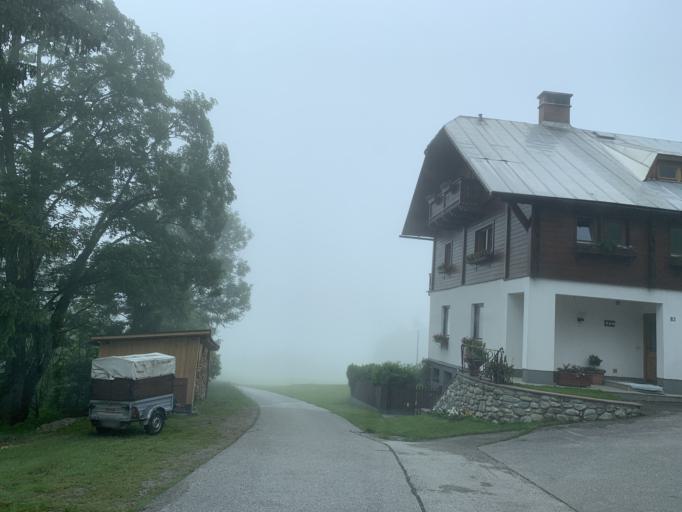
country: AT
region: Styria
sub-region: Politischer Bezirk Liezen
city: Schladming
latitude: 47.3930
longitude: 13.6195
